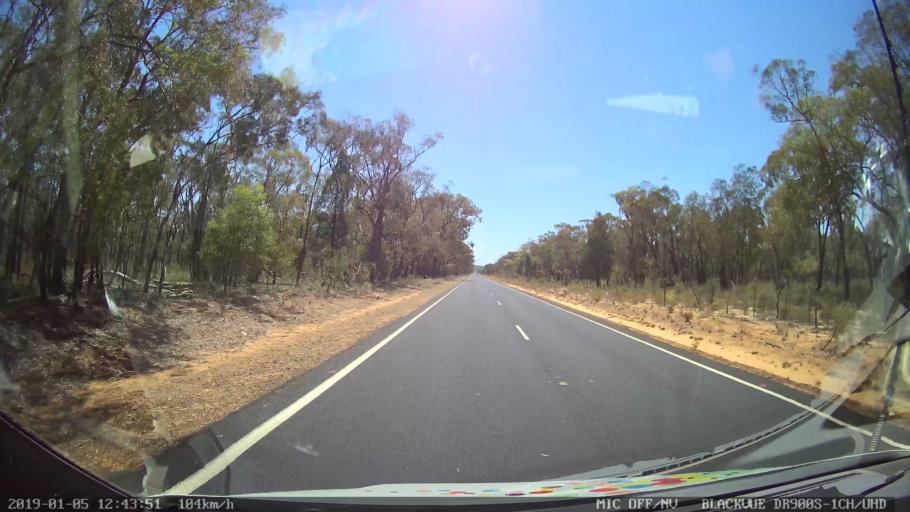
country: AU
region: New South Wales
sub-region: Warrumbungle Shire
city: Coonabarabran
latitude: -31.1438
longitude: 149.5296
